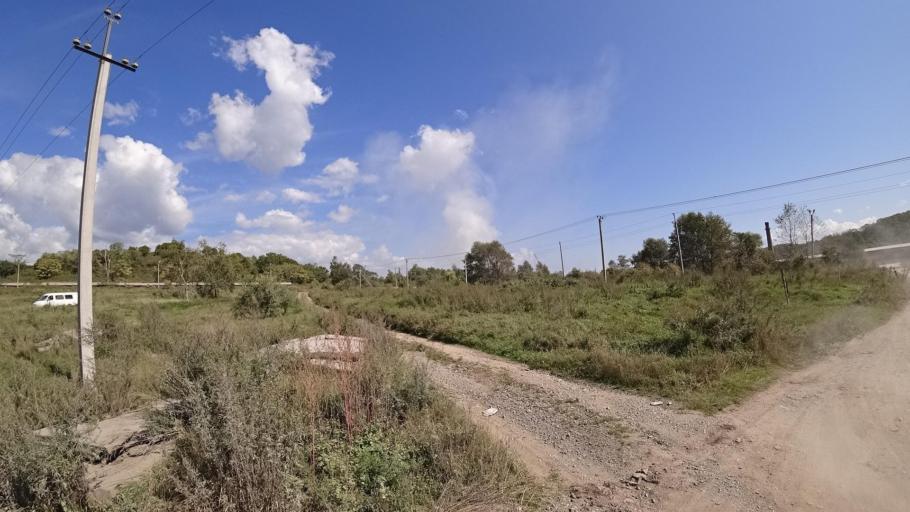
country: RU
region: Jewish Autonomous Oblast
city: Londoko
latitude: 49.0063
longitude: 131.8899
